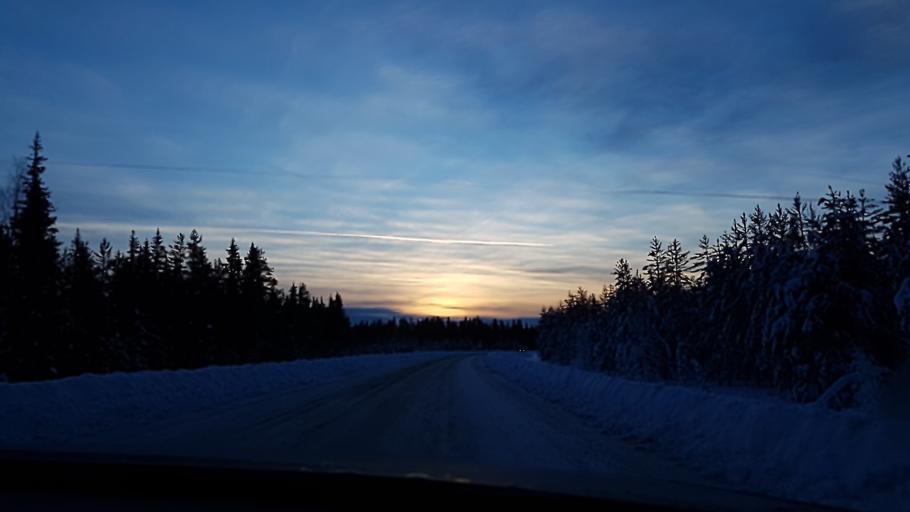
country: SE
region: Norrbotten
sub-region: Jokkmokks Kommun
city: Jokkmokk
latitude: 66.0712
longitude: 20.0765
